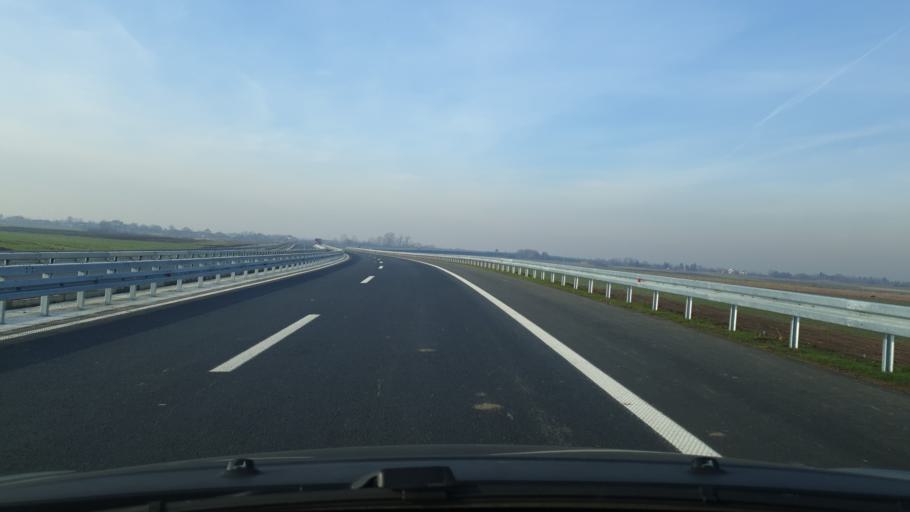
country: RS
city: Boljevci
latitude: 44.7248
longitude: 20.2551
